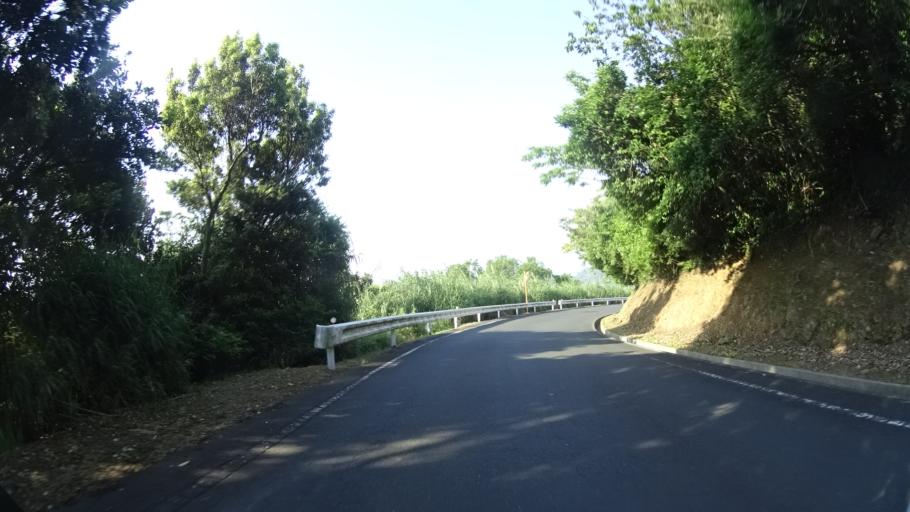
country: JP
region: Ehime
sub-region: Nishiuwa-gun
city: Ikata-cho
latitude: 33.3703
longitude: 132.0571
